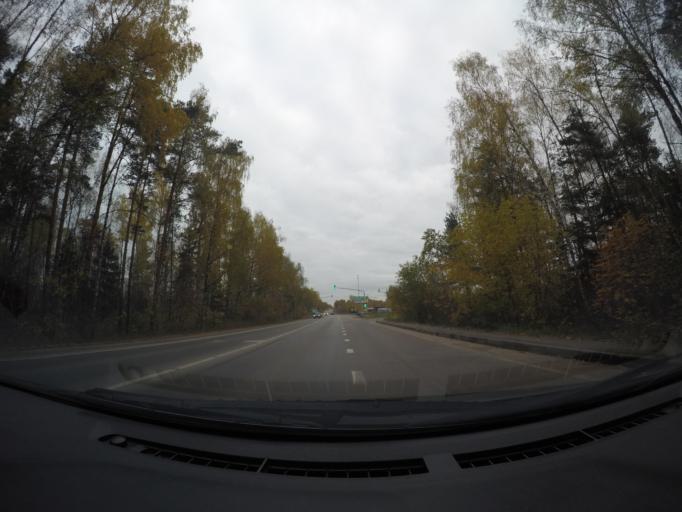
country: RU
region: Moskovskaya
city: Obukhovo
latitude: 55.7808
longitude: 38.2475
